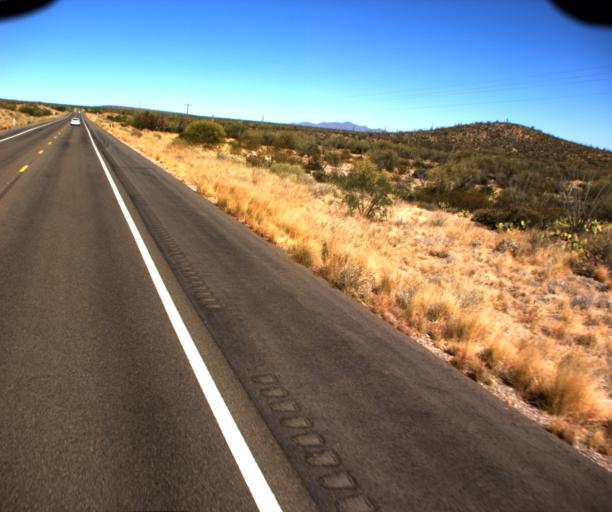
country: US
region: Arizona
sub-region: Pima County
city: Three Points
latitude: 32.0375
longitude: -111.5141
